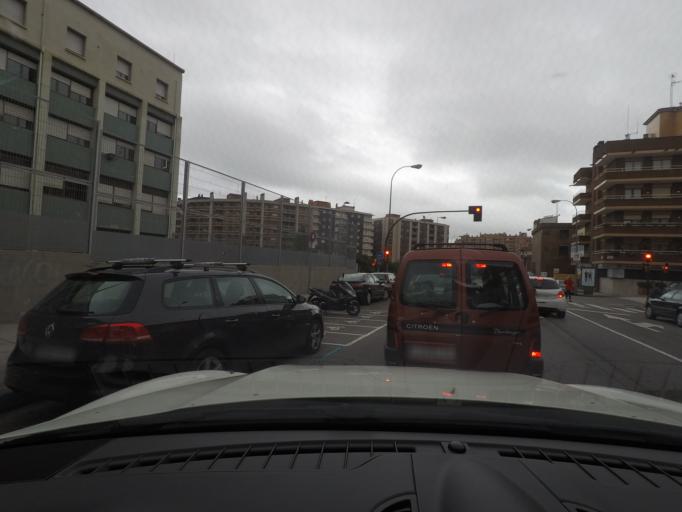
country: ES
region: Asturias
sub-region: Province of Asturias
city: Gijon
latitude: 43.5354
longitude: -5.6487
